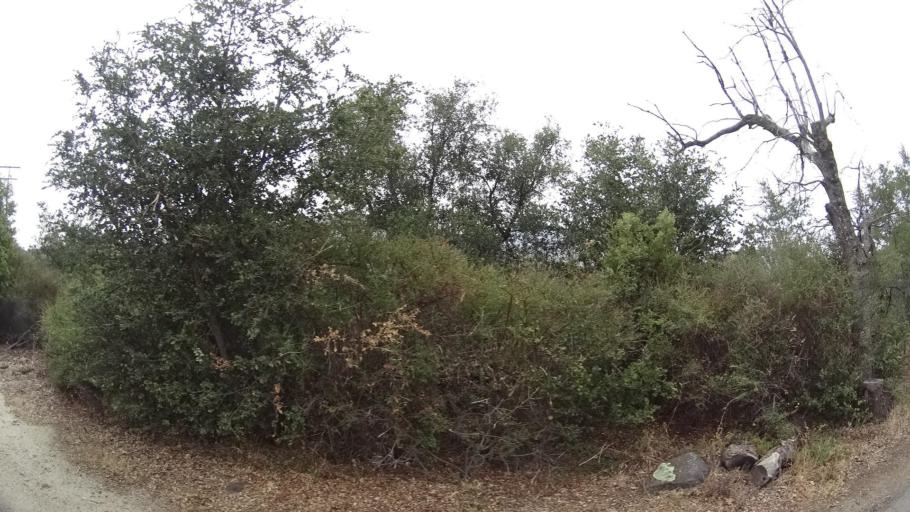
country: US
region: California
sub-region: San Diego County
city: Julian
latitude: 33.0417
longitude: -116.6255
